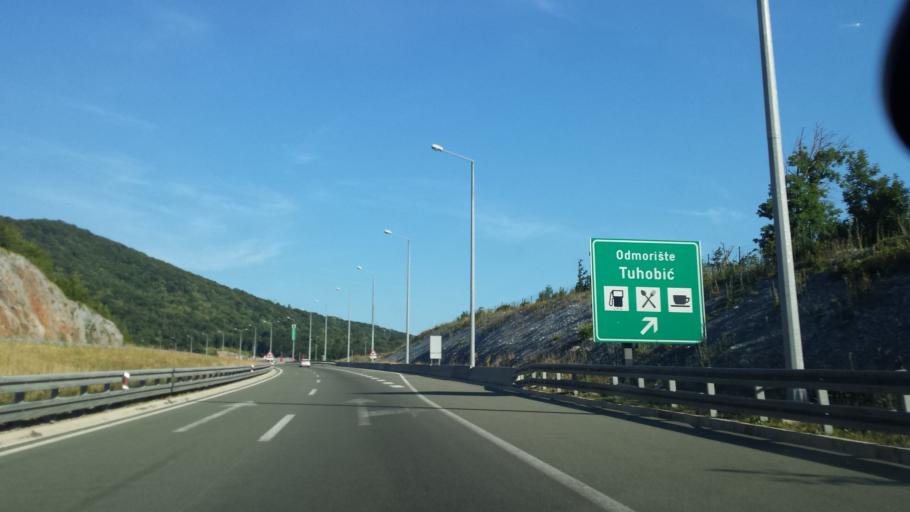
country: HR
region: Primorsko-Goranska
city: Hreljin
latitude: 45.3252
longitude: 14.6211
